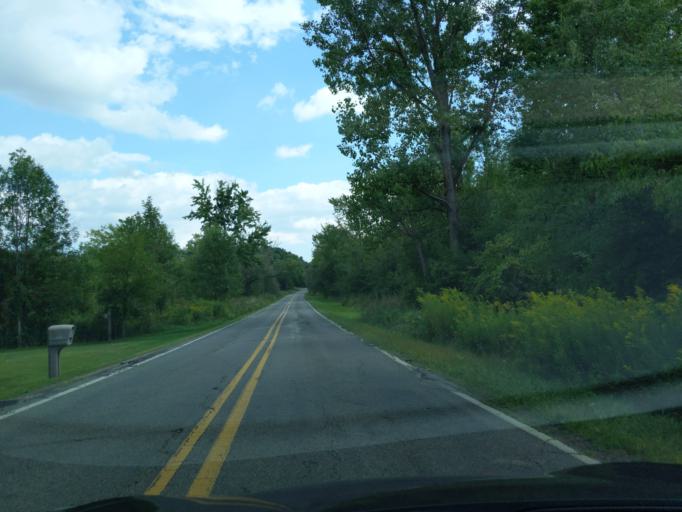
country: US
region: Michigan
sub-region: Jackson County
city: Spring Arbor
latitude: 42.3231
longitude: -84.5312
